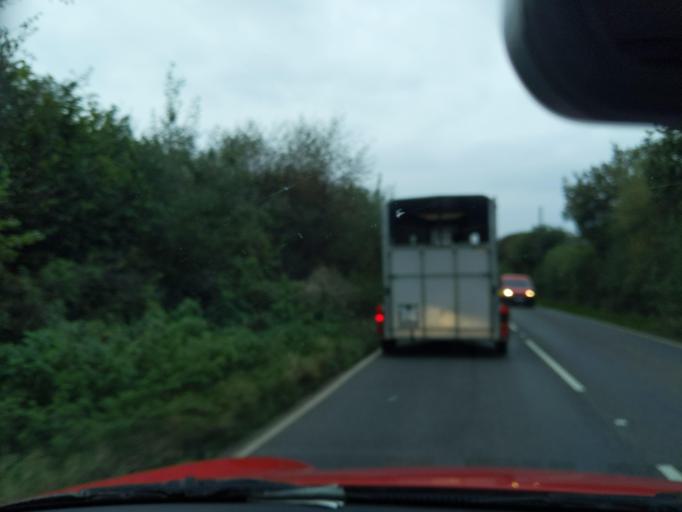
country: GB
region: England
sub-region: Devon
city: Okehampton
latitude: 50.7869
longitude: -4.0330
